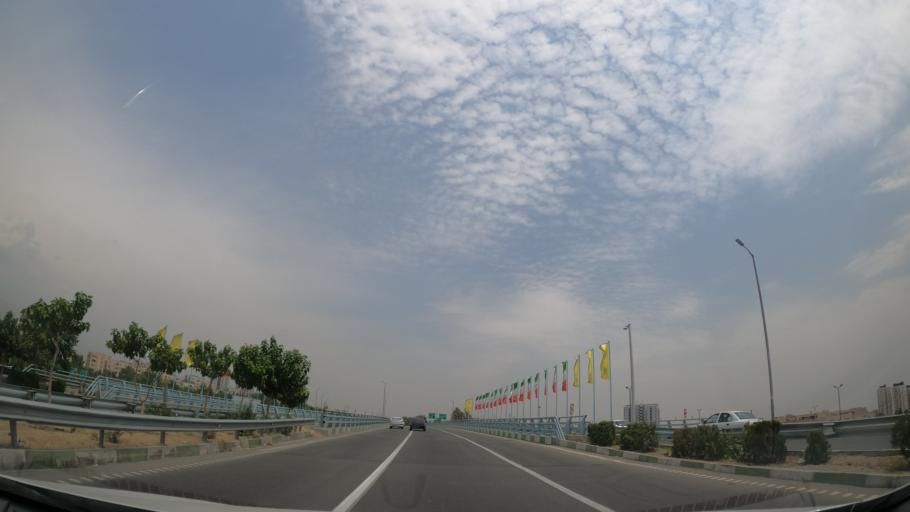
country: IR
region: Tehran
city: Shahr-e Qods
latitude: 35.7390
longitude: 51.2531
